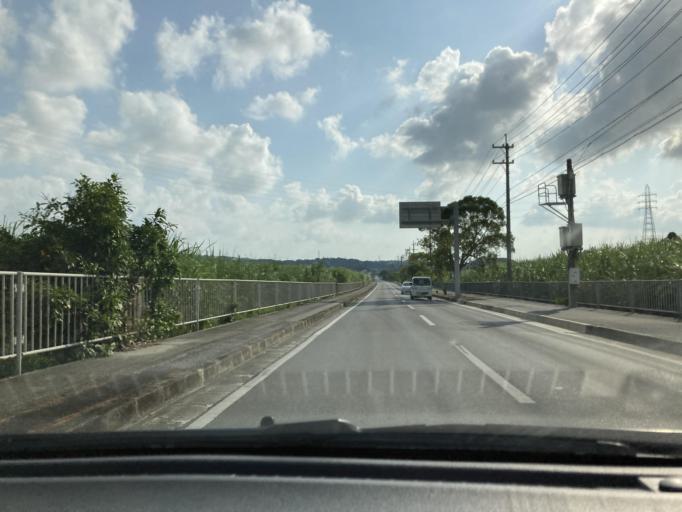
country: JP
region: Okinawa
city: Itoman
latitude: 26.1485
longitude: 127.7071
